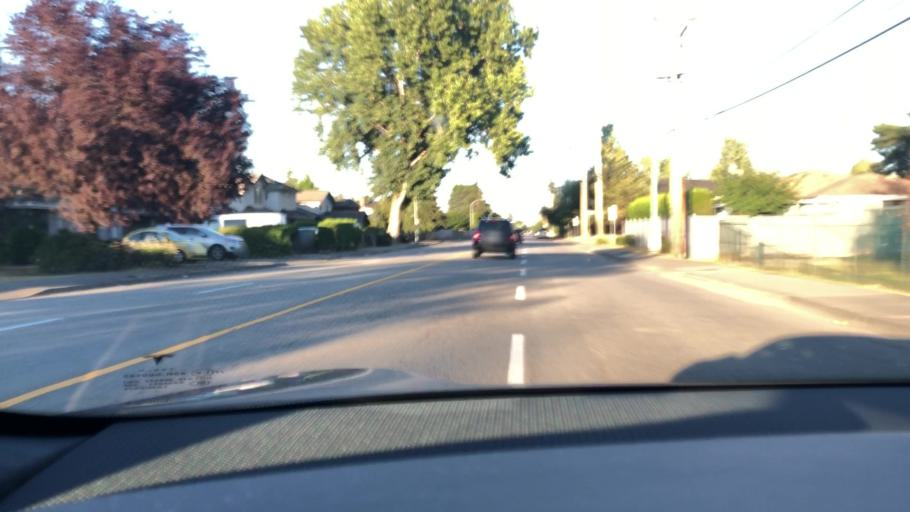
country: CA
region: British Columbia
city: Richmond
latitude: 49.1483
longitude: -123.1760
